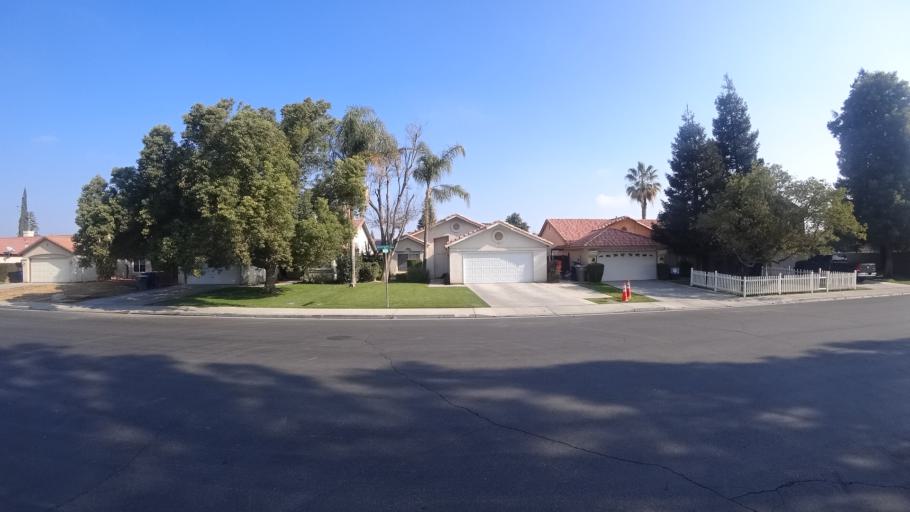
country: US
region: California
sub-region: Kern County
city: Greenacres
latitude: 35.3053
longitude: -119.0848
